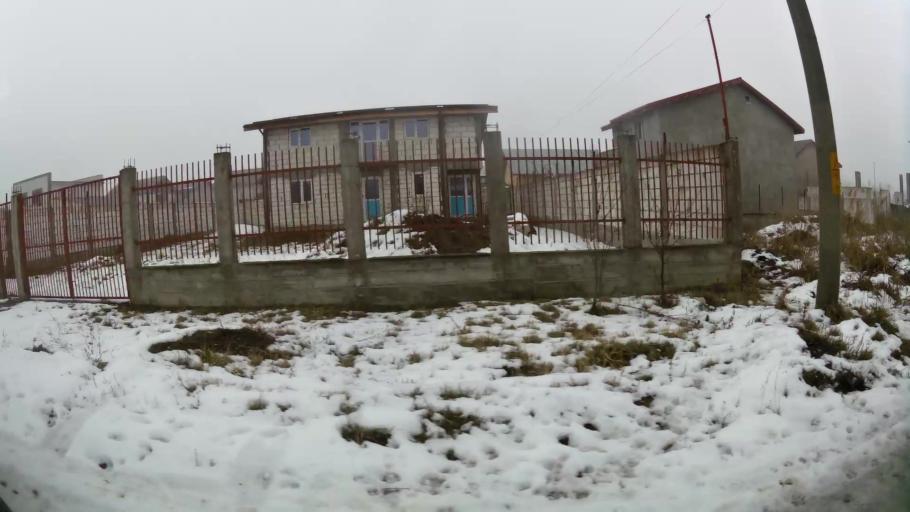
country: RO
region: Ilfov
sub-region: Comuna Chitila
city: Rudeni
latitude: 44.4687
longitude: 25.9805
